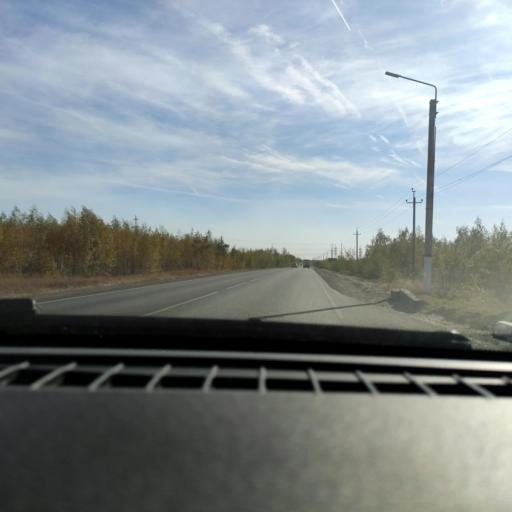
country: RU
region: Voronezj
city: Maslovka
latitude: 51.5862
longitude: 39.2554
